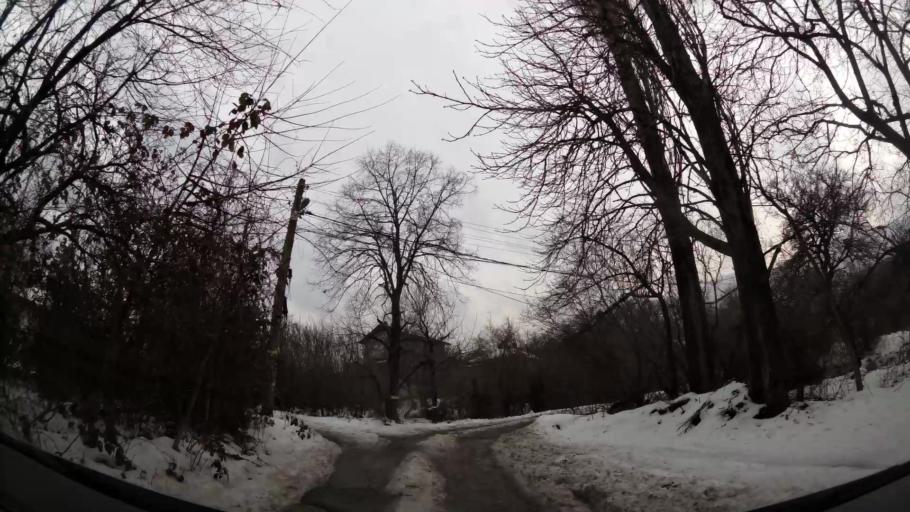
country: BG
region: Sofia-Capital
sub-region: Stolichna Obshtina
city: Sofia
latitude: 42.6509
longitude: 23.2313
